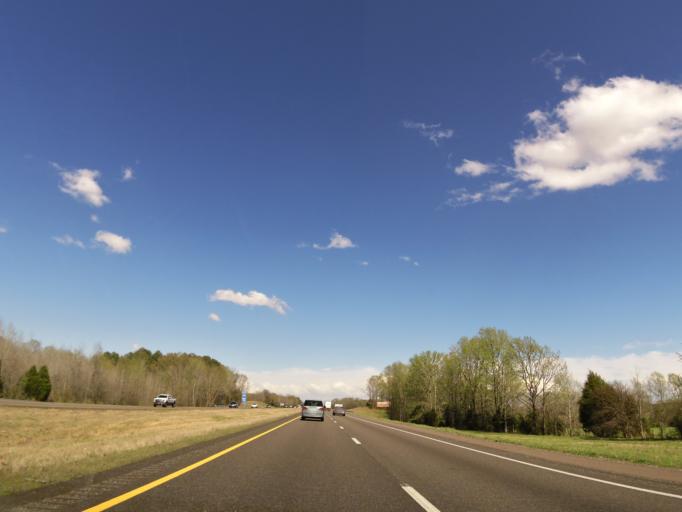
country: US
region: Tennessee
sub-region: Henderson County
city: Lexington
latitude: 35.7600
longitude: -88.4894
